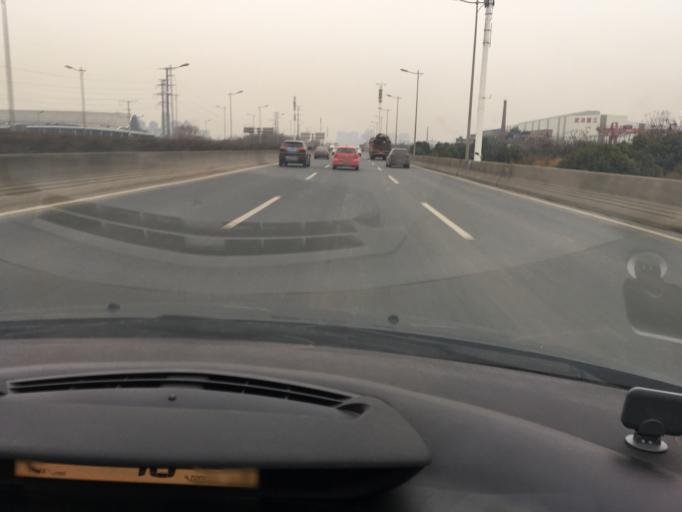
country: CN
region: Hubei
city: Hongqi
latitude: 30.6029
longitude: 114.4261
